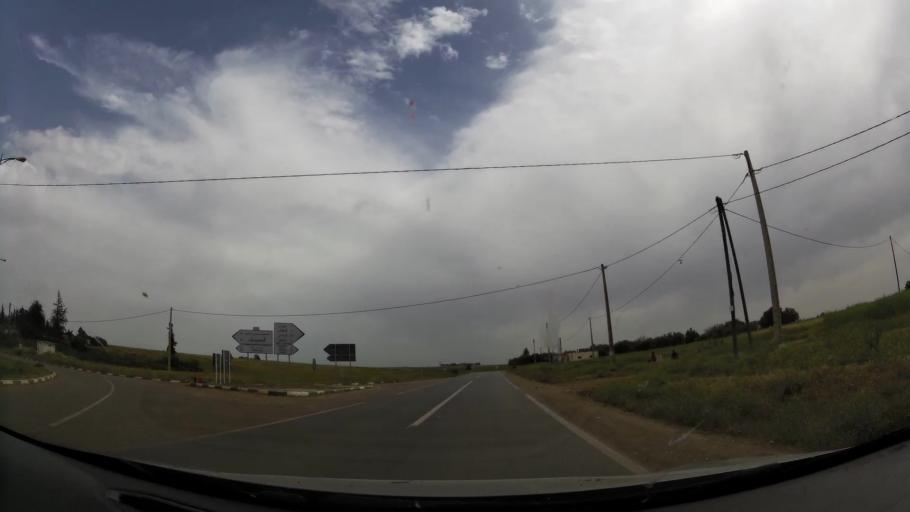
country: MA
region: Rabat-Sale-Zemmour-Zaer
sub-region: Khemisset
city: Tiflet
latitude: 33.8002
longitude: -6.2724
